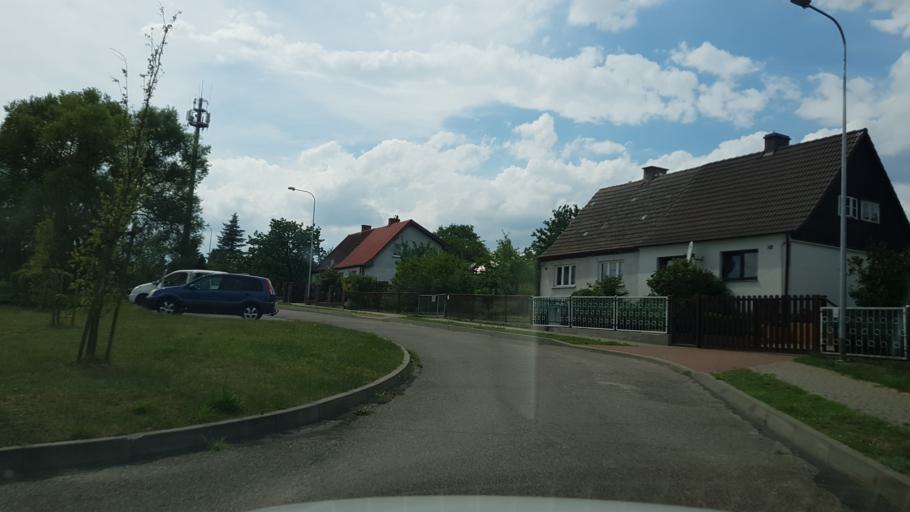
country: PL
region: West Pomeranian Voivodeship
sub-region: Powiat drawski
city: Drawsko Pomorskie
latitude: 53.5428
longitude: 15.8081
